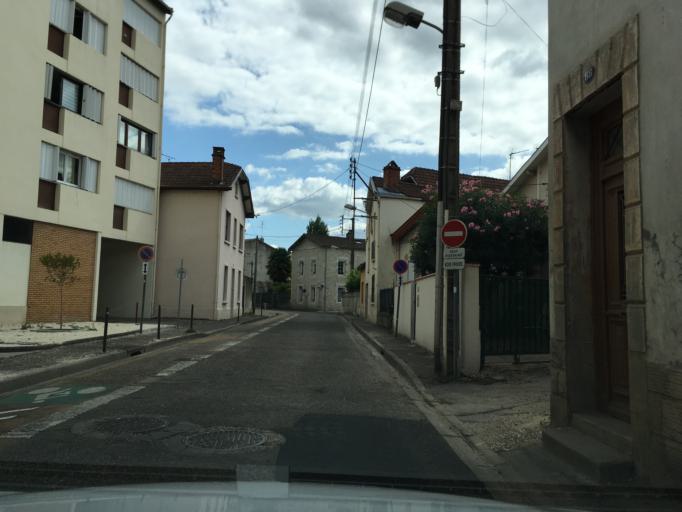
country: FR
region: Aquitaine
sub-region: Departement du Lot-et-Garonne
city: Agen
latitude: 44.2008
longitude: 0.6288
